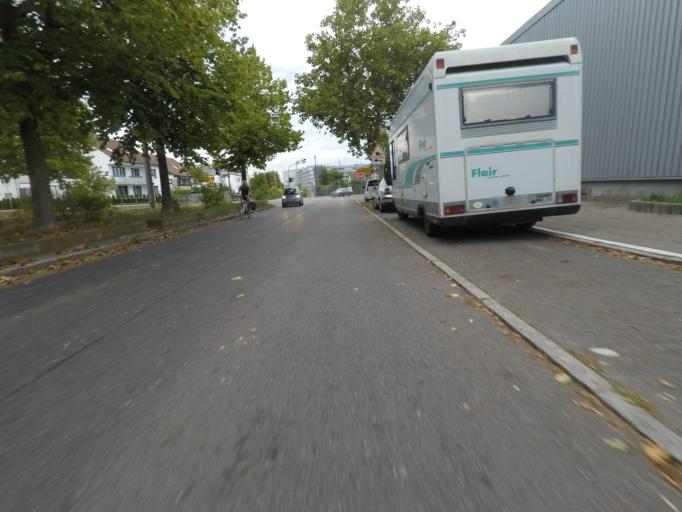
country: DE
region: Baden-Wuerttemberg
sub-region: Regierungsbezirk Stuttgart
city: Leinfelden-Echterdingen
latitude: 48.7050
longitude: 9.1435
